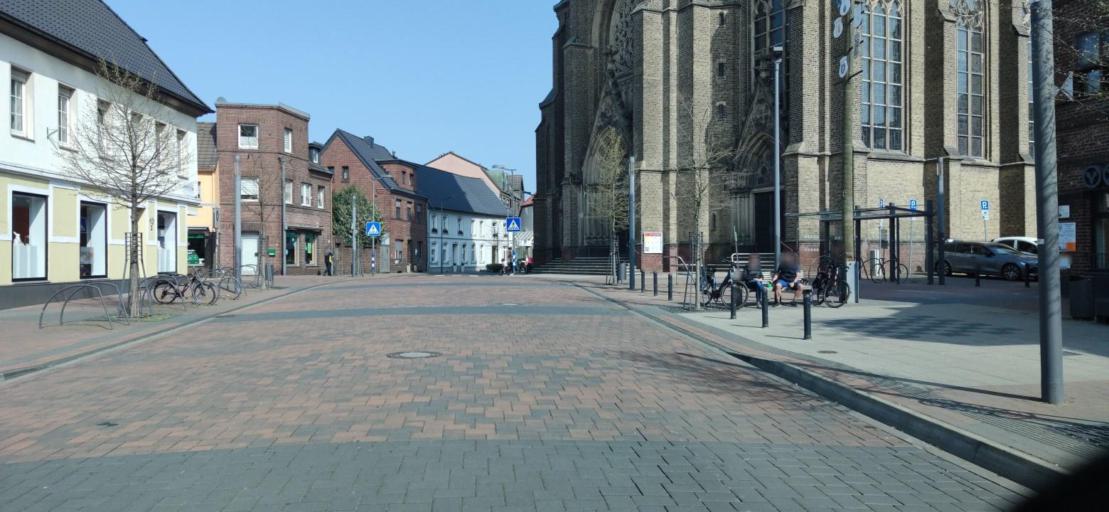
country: DE
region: North Rhine-Westphalia
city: Tonisvorst
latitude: 51.2783
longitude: 6.4622
